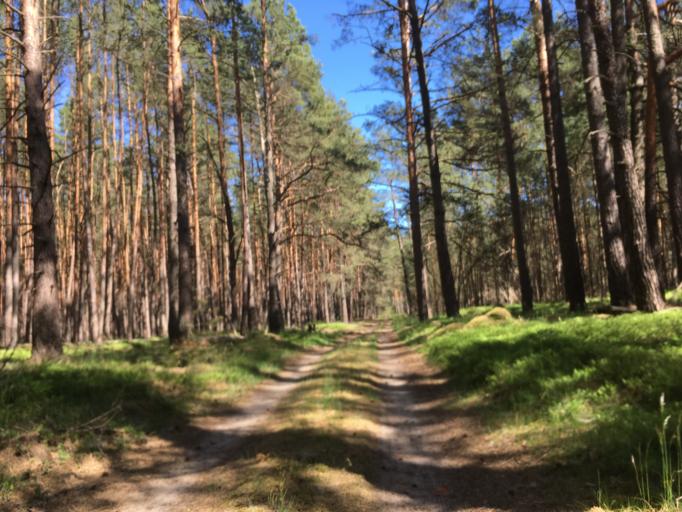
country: DE
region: Brandenburg
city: Friedrichswalde
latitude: 52.9655
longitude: 13.6527
